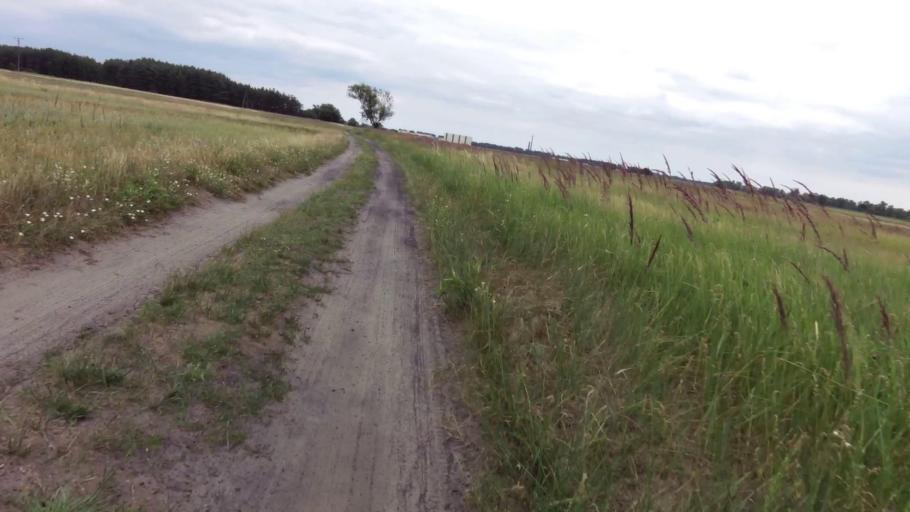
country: PL
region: Lubusz
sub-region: Powiat gorzowski
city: Kostrzyn nad Odra
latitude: 52.6175
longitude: 14.5941
